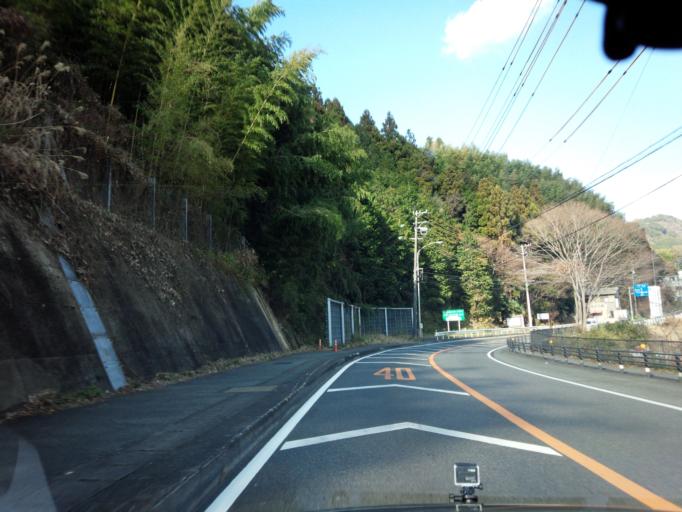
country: JP
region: Shizuoka
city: Fujinomiya
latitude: 35.0937
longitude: 138.5139
